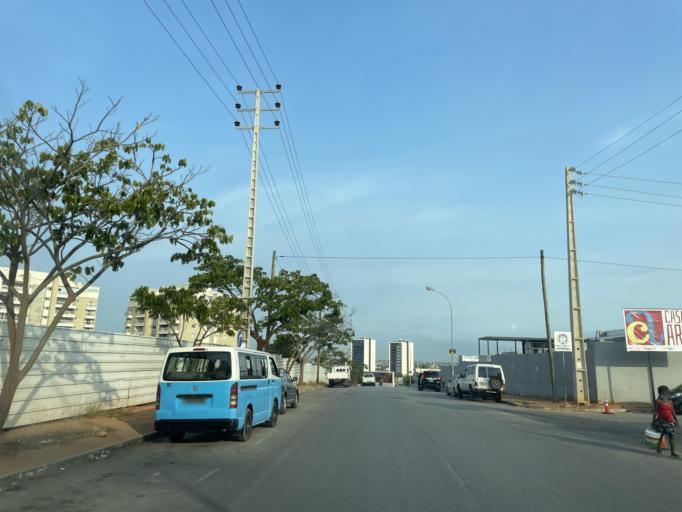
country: AO
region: Luanda
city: Luanda
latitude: -8.9182
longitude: 13.1955
